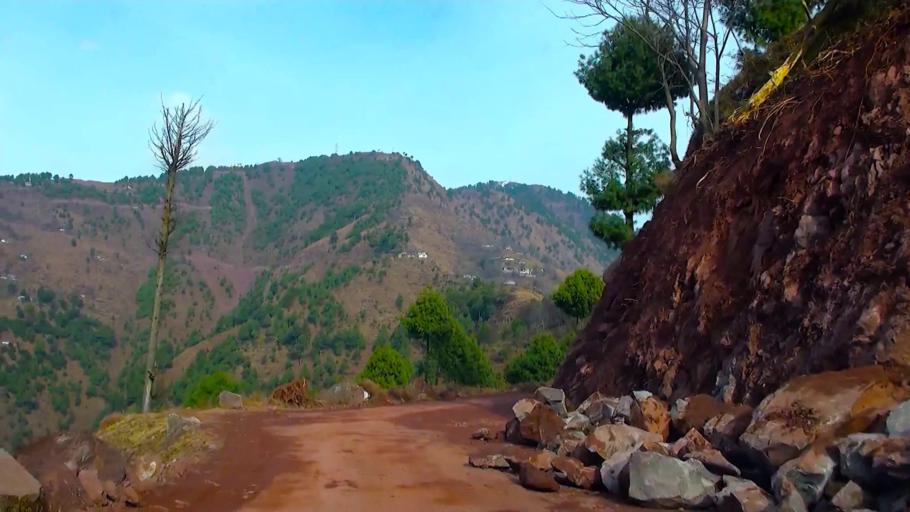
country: PK
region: Azad Kashmir
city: Muzaffarabad
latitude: 34.3704
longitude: 73.5146
